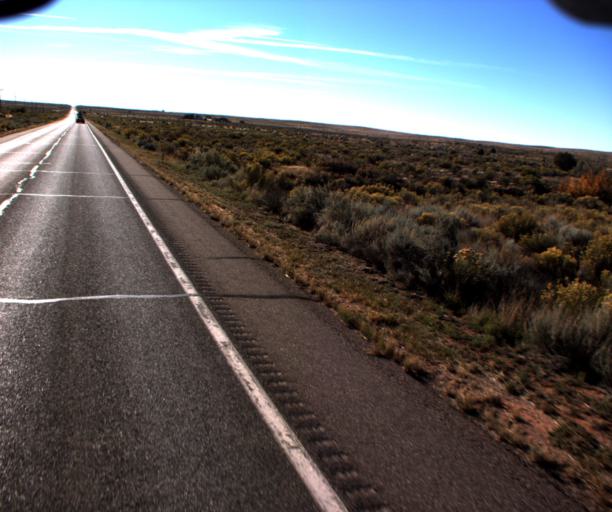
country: US
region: Arizona
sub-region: Mohave County
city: Colorado City
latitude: 36.9295
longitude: -112.9425
